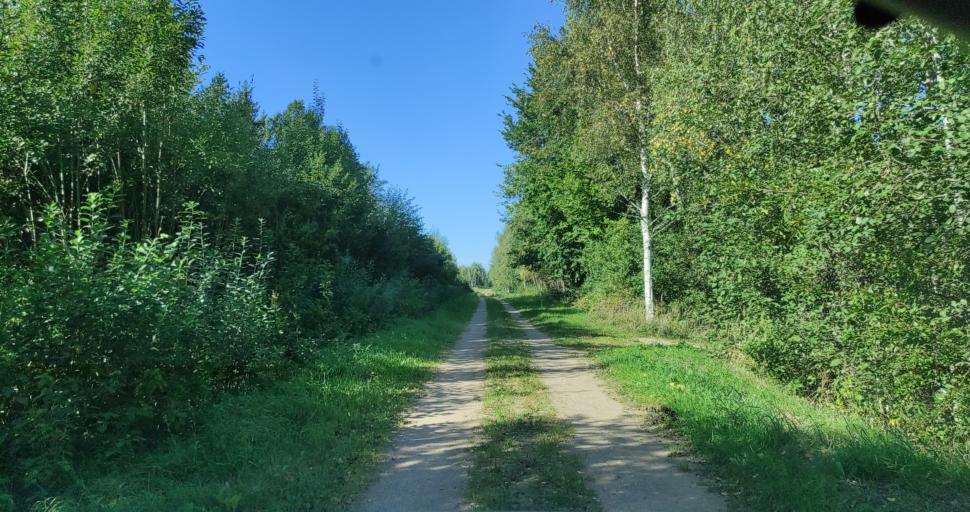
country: LV
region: Kuldigas Rajons
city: Kuldiga
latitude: 56.9744
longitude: 21.9219
